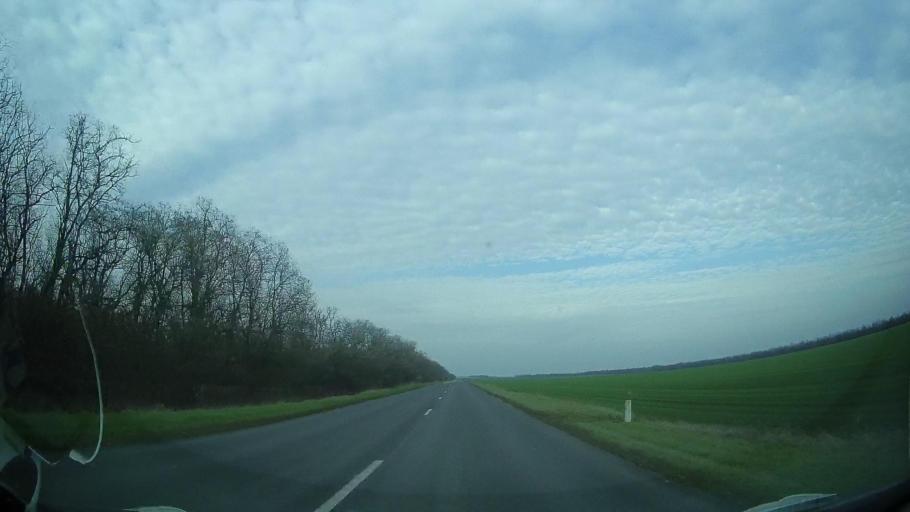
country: RU
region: Rostov
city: Zernograd
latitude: 46.9495
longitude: 40.3667
